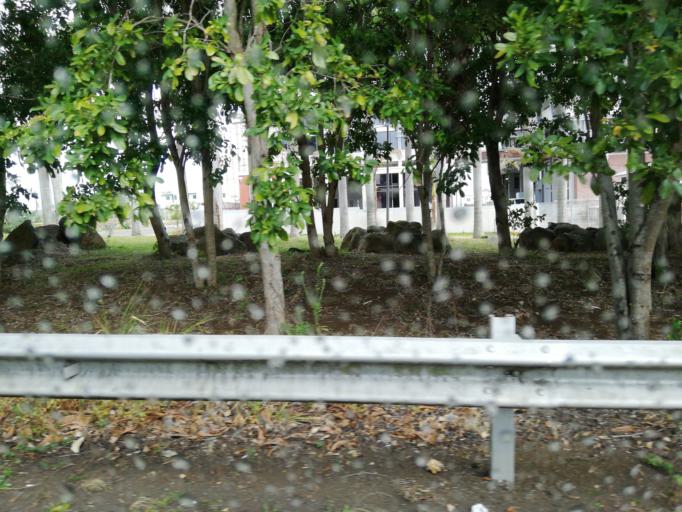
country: MU
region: Plaines Wilhems
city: Ebene
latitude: -20.2418
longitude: 57.4838
